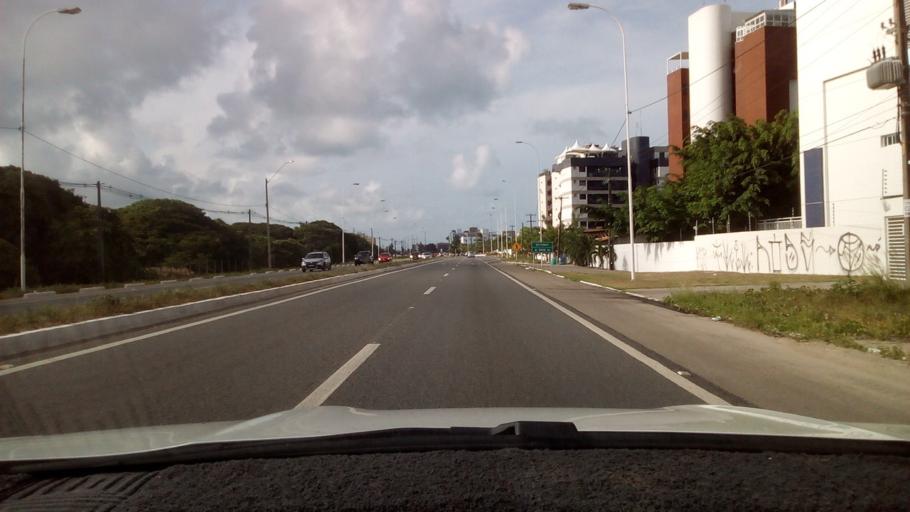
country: BR
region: Paraiba
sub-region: Cabedelo
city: Cabedelo
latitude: -6.9978
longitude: -34.8282
